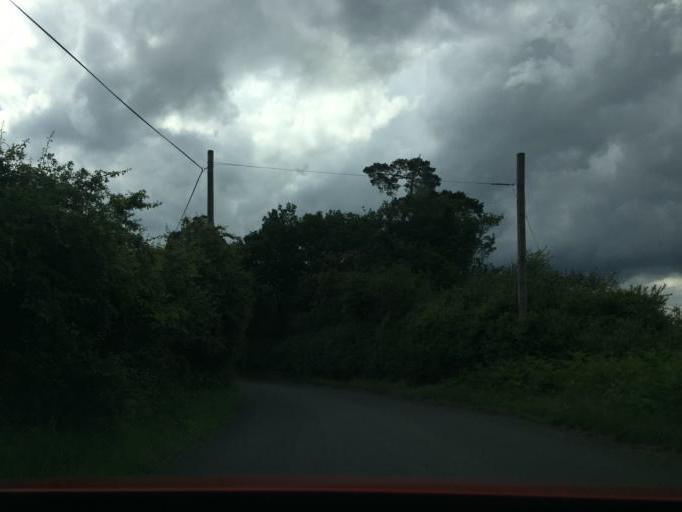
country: GB
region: England
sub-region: Hertfordshire
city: Harpenden
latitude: 51.8607
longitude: -0.3500
